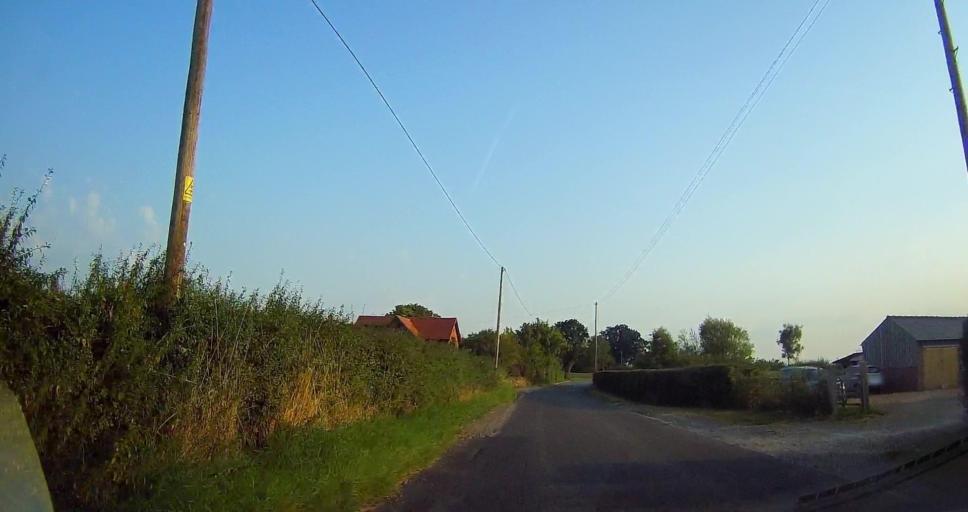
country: GB
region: England
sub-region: Cheshire East
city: Nantwich
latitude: 53.0134
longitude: -2.5239
